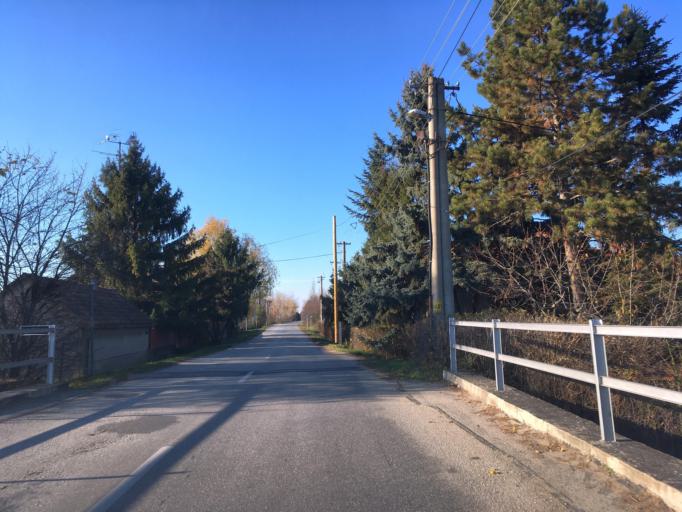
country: SK
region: Nitriansky
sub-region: Okres Komarno
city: Hurbanovo
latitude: 47.8899
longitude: 18.1988
